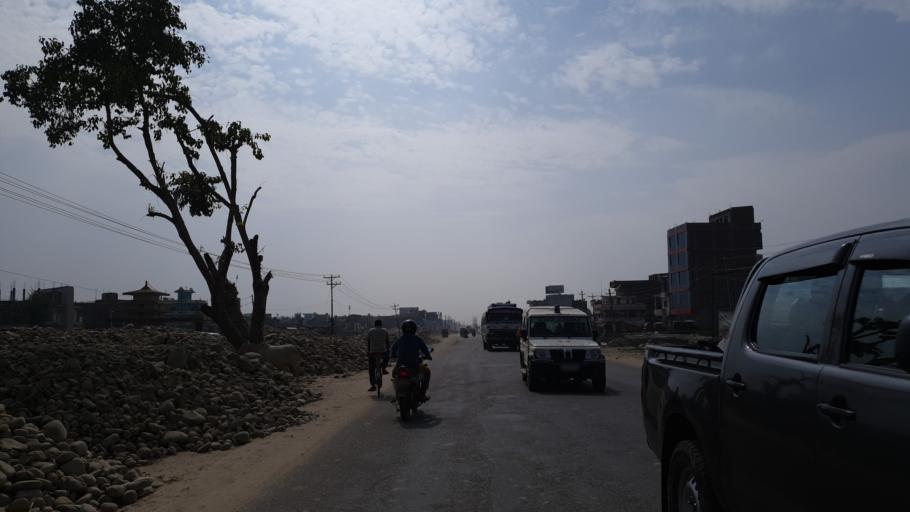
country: NP
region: Central Region
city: Janakpur
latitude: 26.7479
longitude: 85.9236
